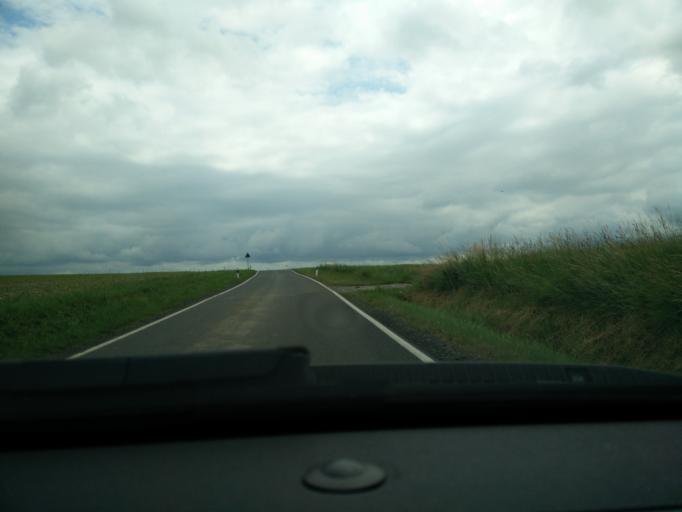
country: DE
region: Saxony
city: Bad Lausick
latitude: 51.1144
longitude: 12.6590
